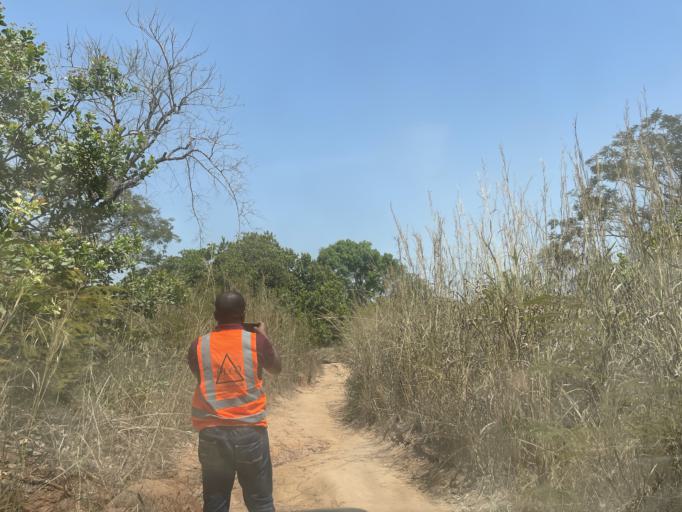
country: GW
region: Oio
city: Bissora
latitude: 12.4187
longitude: -15.6178
